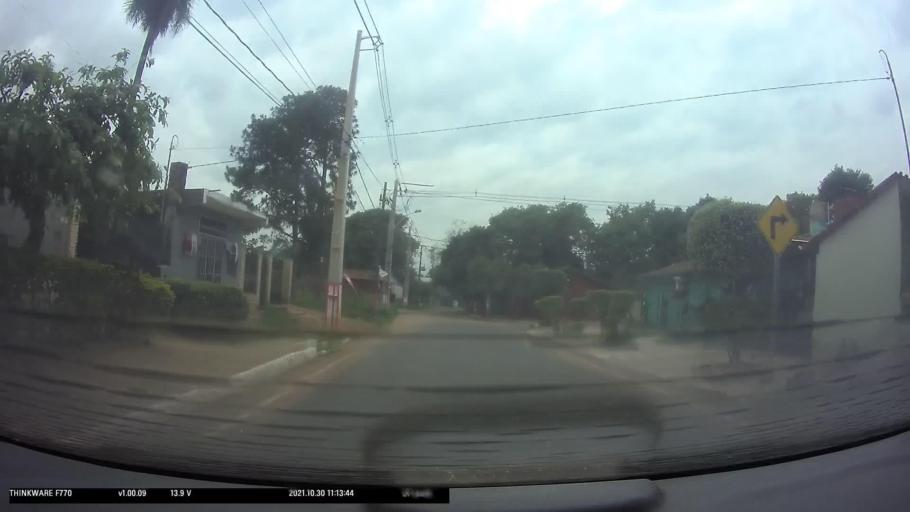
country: PY
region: Central
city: San Lorenzo
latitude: -25.3088
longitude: -57.5100
